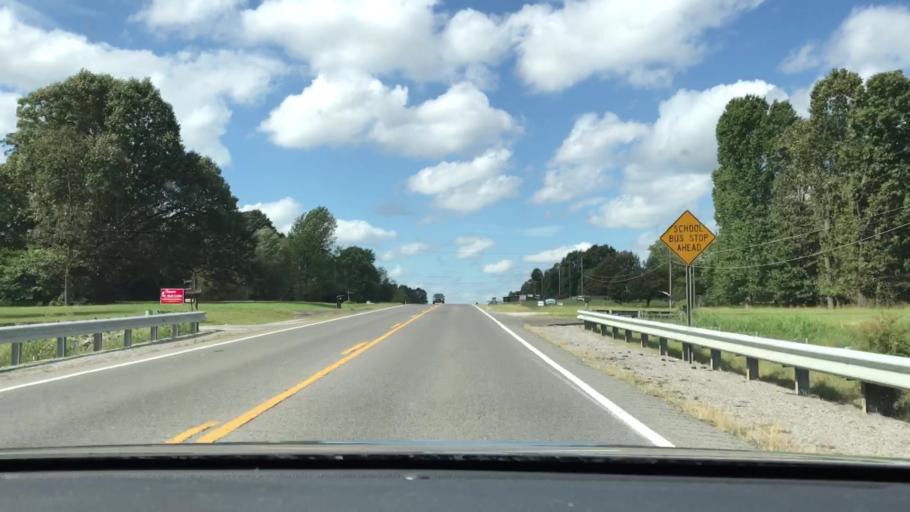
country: US
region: Kentucky
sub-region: Livingston County
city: Ledbetter
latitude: 37.0072
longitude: -88.4728
